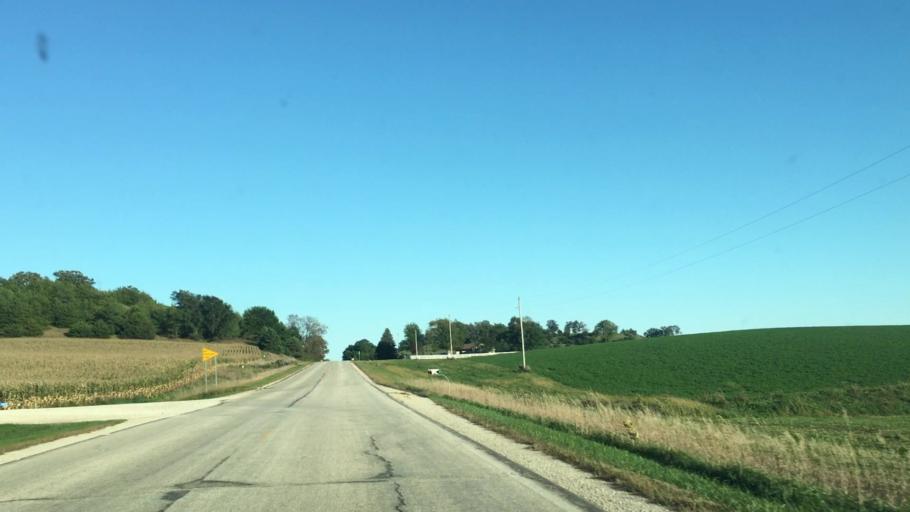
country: US
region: Minnesota
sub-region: Fillmore County
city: Chatfield
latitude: 43.8424
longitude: -92.0896
